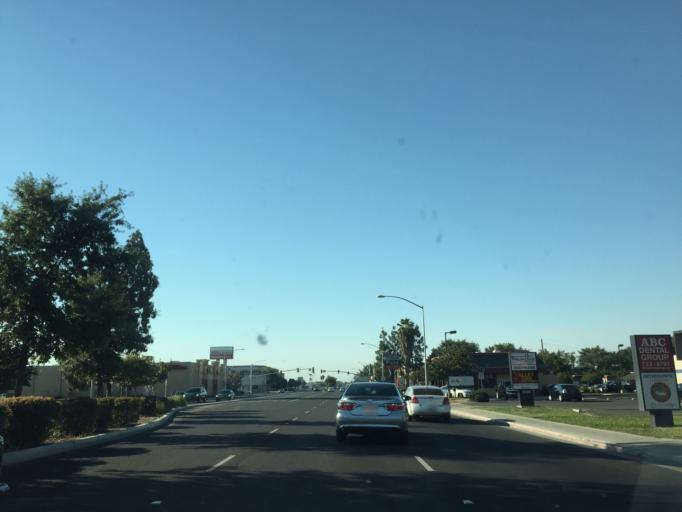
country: US
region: California
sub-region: Tulare County
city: Visalia
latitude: 36.3074
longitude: -119.3137
